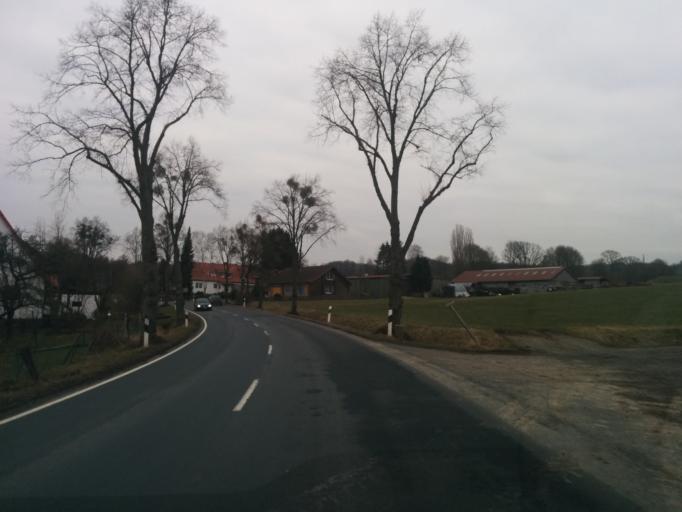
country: DE
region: Lower Saxony
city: Waake
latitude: 51.5955
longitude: 10.0271
